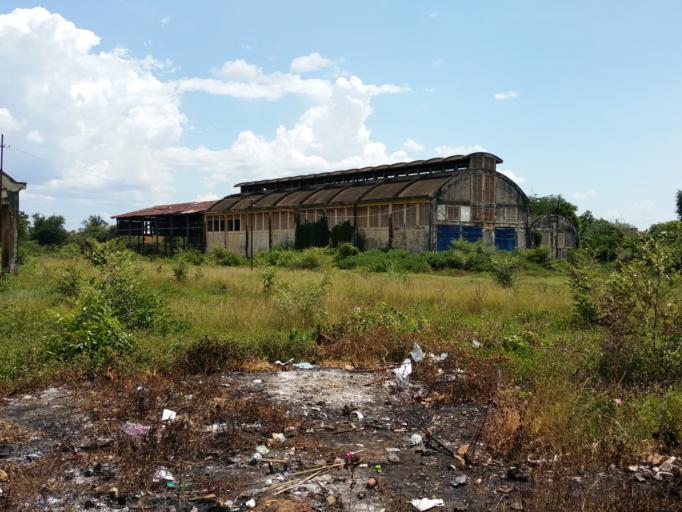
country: KH
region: Battambang
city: Battambang
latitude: 13.0973
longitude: 103.1945
